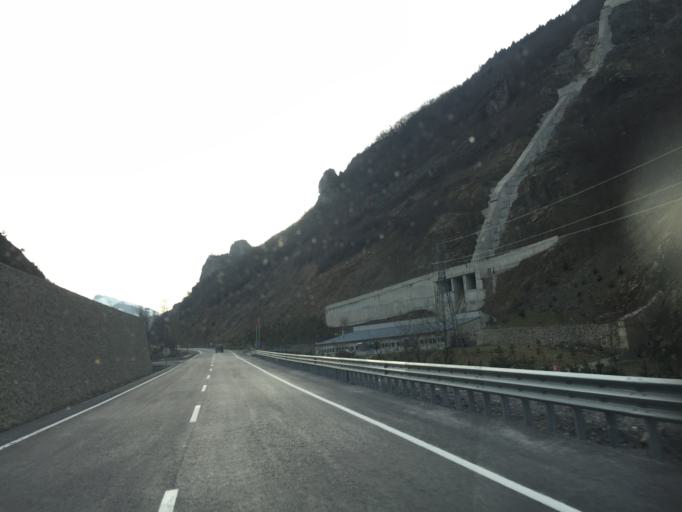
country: TR
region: Trabzon
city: Macka
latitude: 40.7361
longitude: 39.5405
